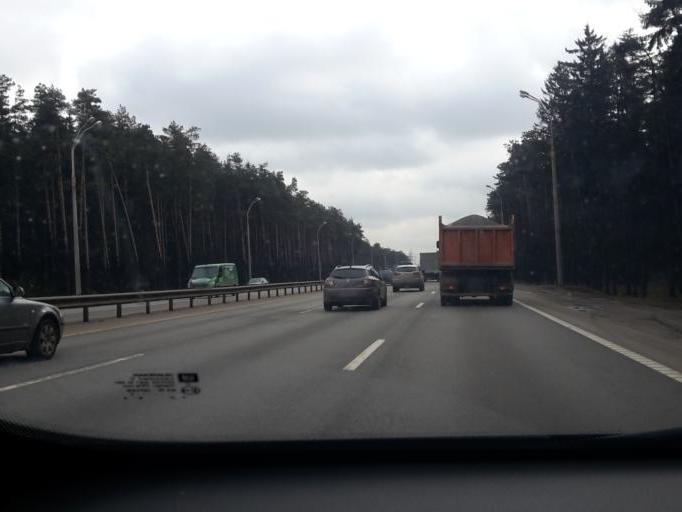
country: BY
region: Minsk
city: Borovlyany
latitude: 53.9499
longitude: 27.6541
